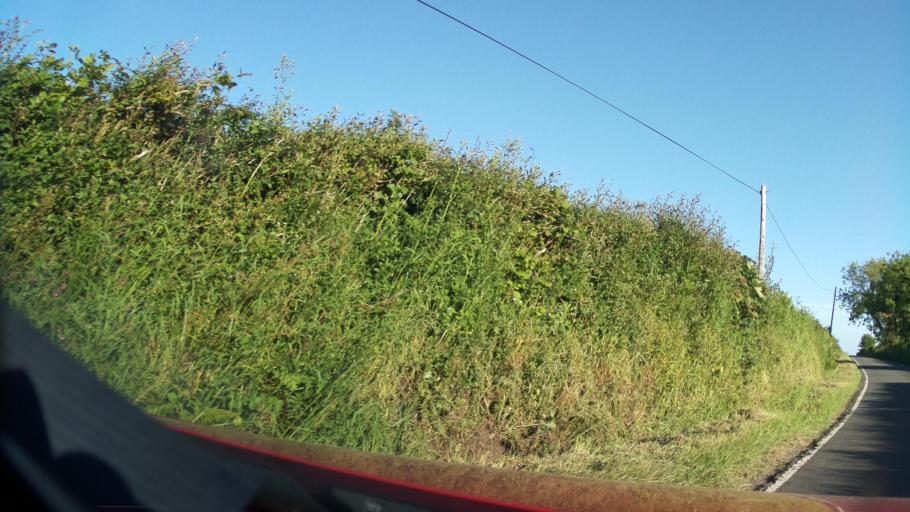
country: GB
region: England
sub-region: Dorset
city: Lyme Regis
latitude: 50.7221
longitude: -2.9906
